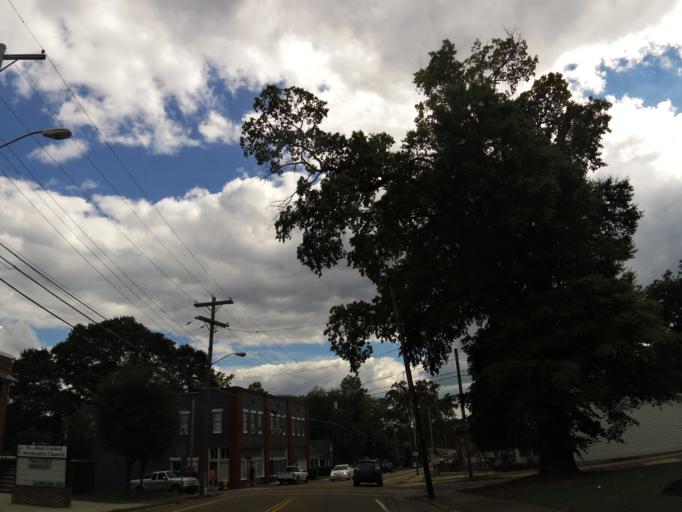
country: US
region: Tennessee
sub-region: Hamilton County
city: Lookout Mountain
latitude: 34.9970
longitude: -85.3297
